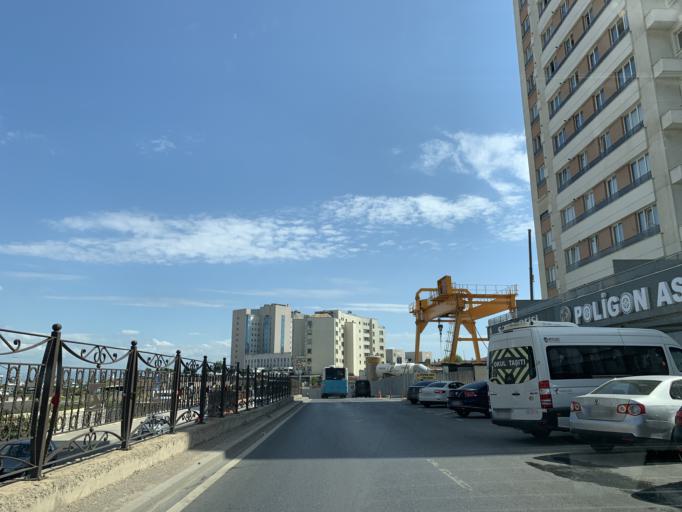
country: TR
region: Istanbul
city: Pendik
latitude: 40.8901
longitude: 29.2629
